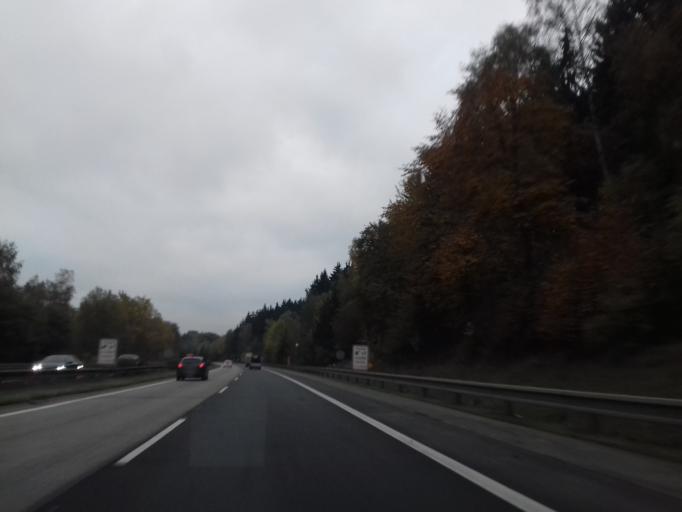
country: CZ
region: Central Bohemia
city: Divisov
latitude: 49.8132
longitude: 14.8809
